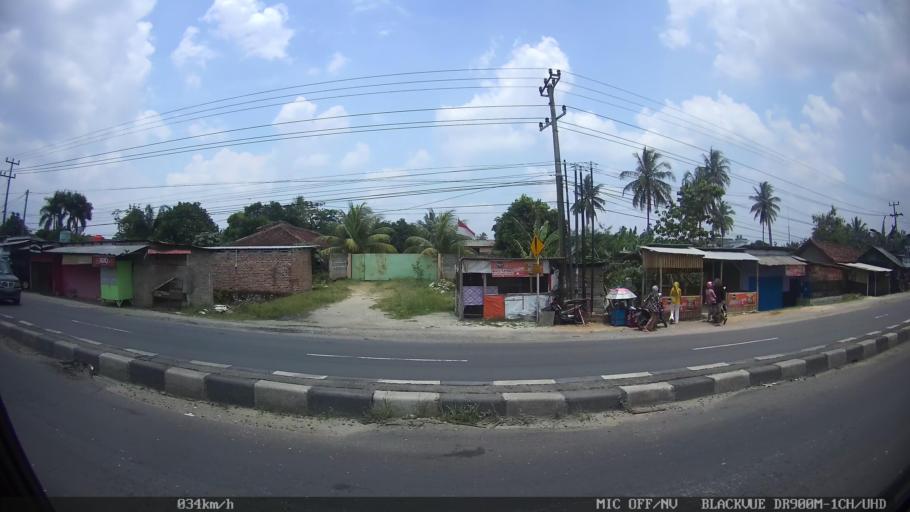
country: ID
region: Lampung
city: Natar
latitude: -5.2836
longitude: 105.1904
